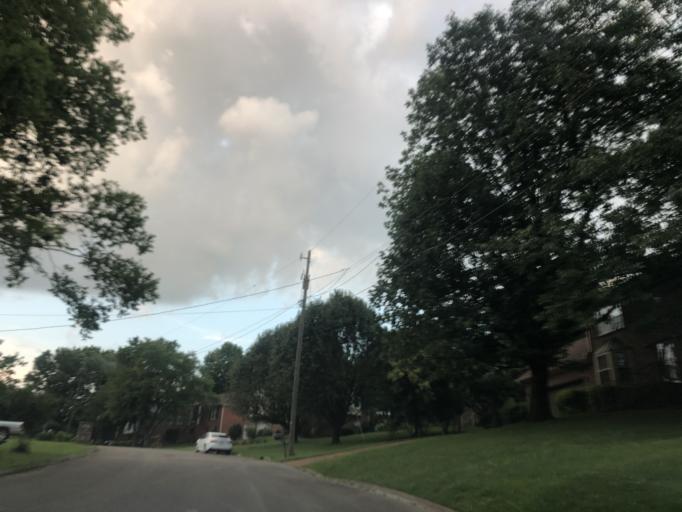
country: US
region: Tennessee
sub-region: Davidson County
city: Lakewood
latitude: 36.1466
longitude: -86.6336
